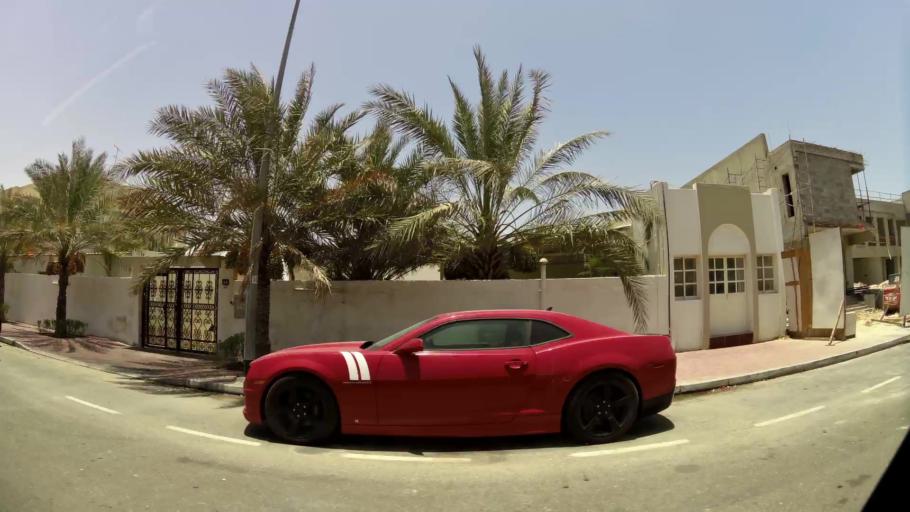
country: AE
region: Dubai
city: Dubai
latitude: 25.1727
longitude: 55.2246
